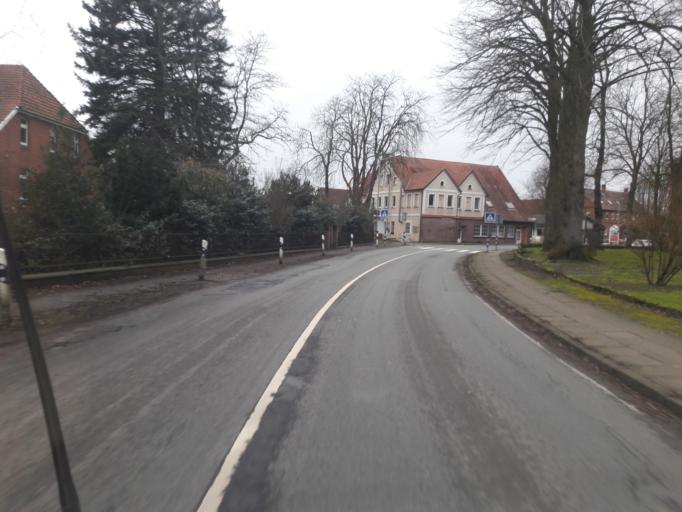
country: DE
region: North Rhine-Westphalia
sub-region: Regierungsbezirk Detmold
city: Minden
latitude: 52.3530
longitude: 8.8522
